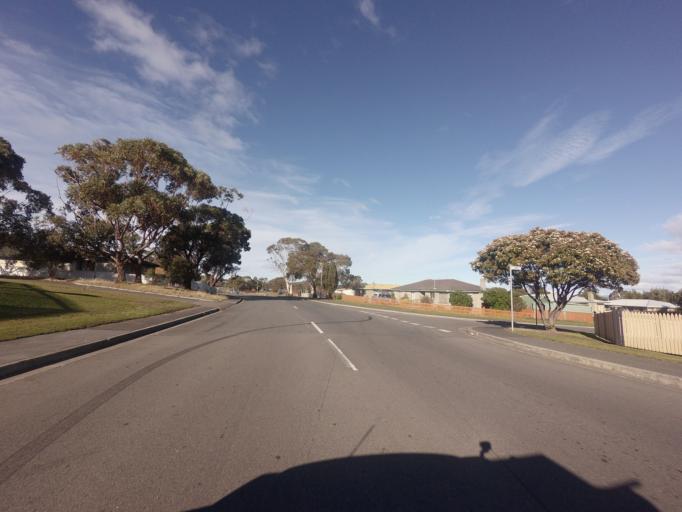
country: AU
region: Tasmania
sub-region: Clarence
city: Rokeby
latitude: -42.8938
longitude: 147.4433
